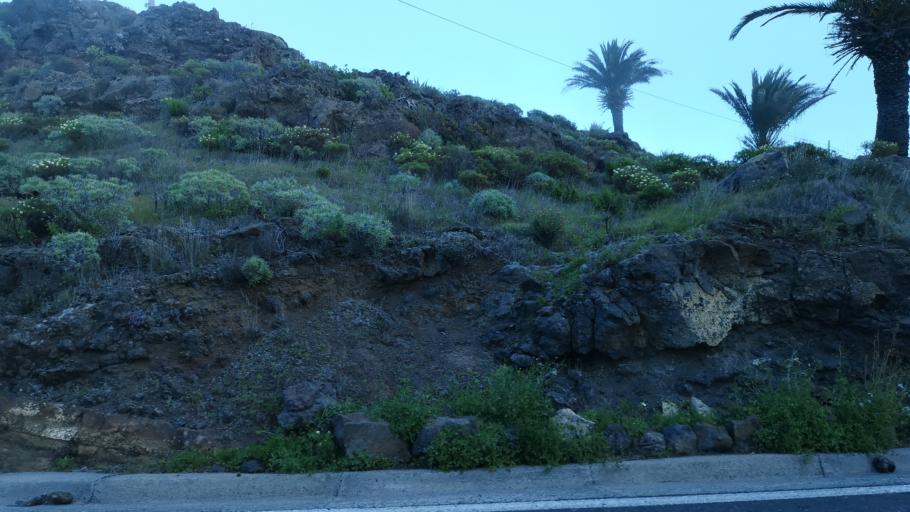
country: ES
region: Canary Islands
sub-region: Provincia de Santa Cruz de Tenerife
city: Alajero
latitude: 28.0778
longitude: -17.2433
